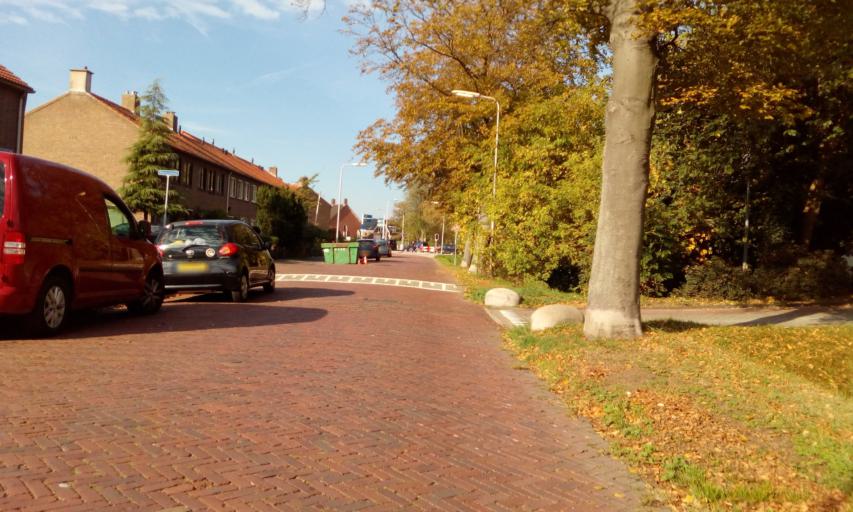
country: NL
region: South Holland
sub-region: Gemeente Westland
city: Naaldwijk
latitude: 51.9899
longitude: 4.2163
